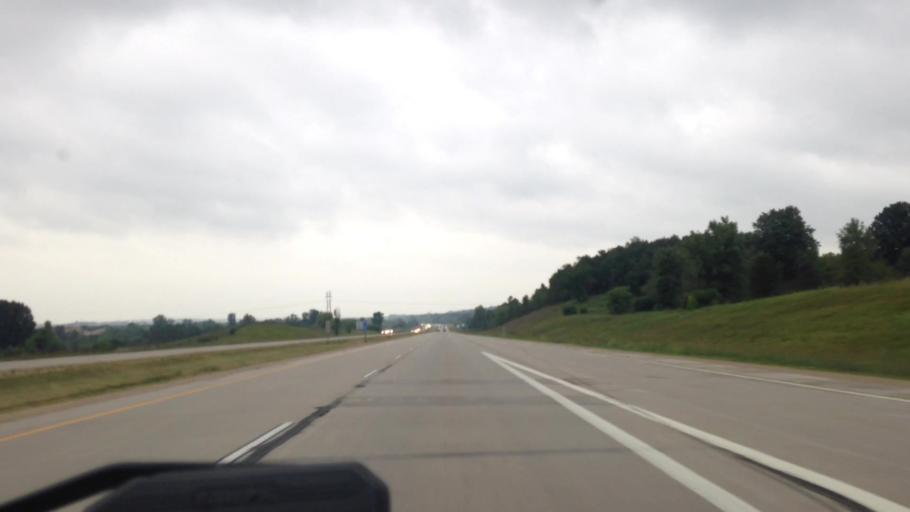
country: US
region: Wisconsin
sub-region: Washington County
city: Slinger
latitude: 43.3746
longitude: -88.3011
